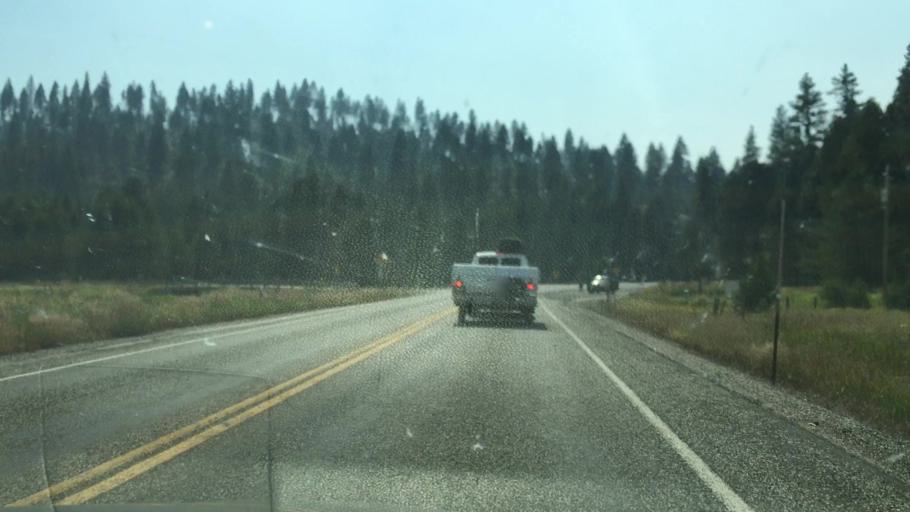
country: US
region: Idaho
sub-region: Valley County
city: Cascade
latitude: 44.3358
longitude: -116.0350
